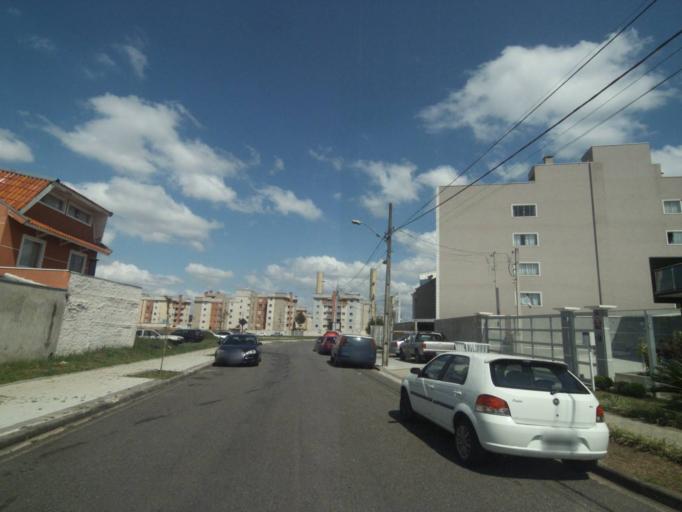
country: BR
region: Parana
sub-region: Curitiba
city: Curitiba
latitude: -25.5016
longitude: -49.3107
